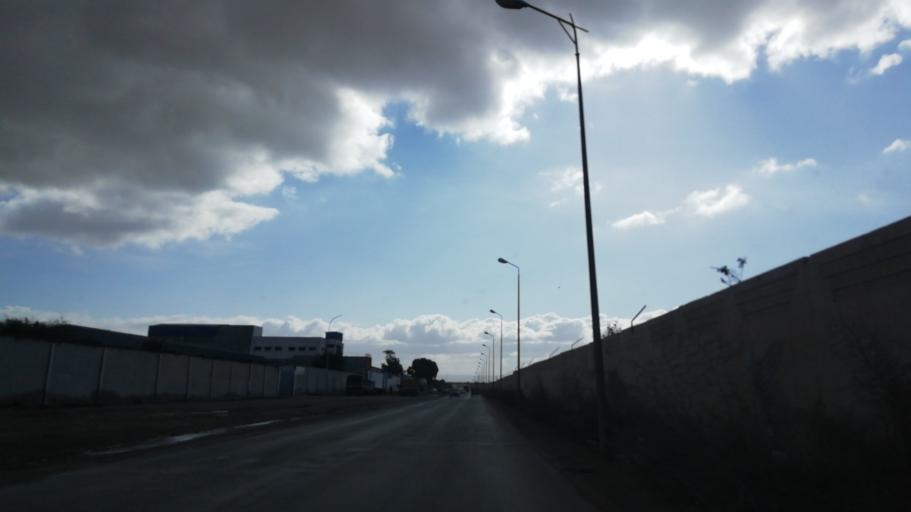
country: DZ
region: Oran
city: Es Senia
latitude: 35.6288
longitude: -0.5925
